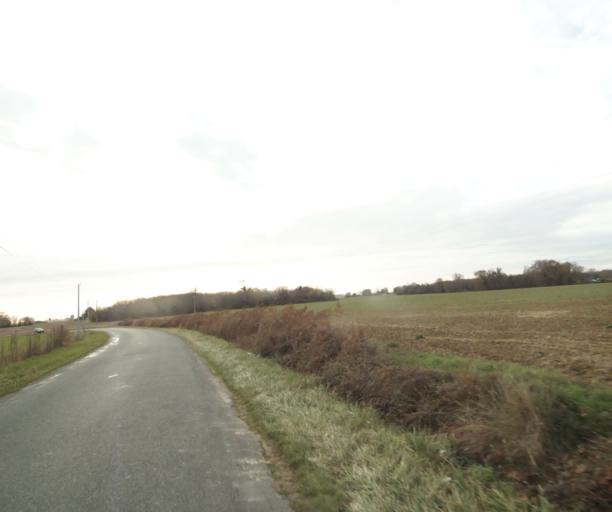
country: FR
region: Poitou-Charentes
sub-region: Departement de la Charente-Maritime
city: Corme-Royal
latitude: 45.7574
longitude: -0.8016
